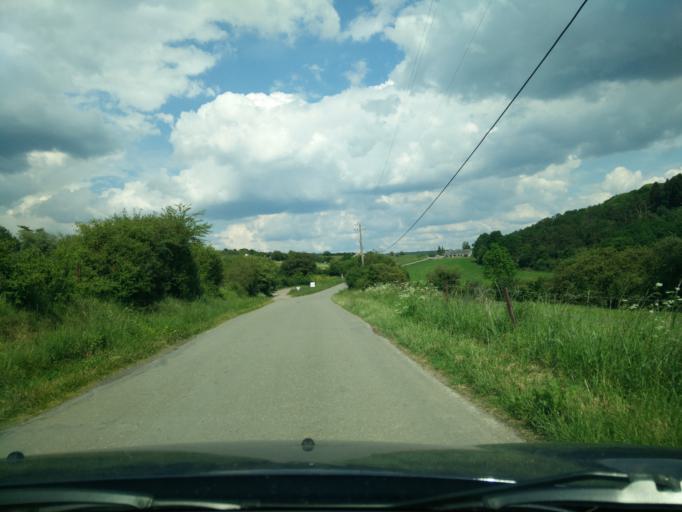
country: BE
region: Wallonia
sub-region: Province de Namur
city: Couvin
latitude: 50.0874
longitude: 4.5755
